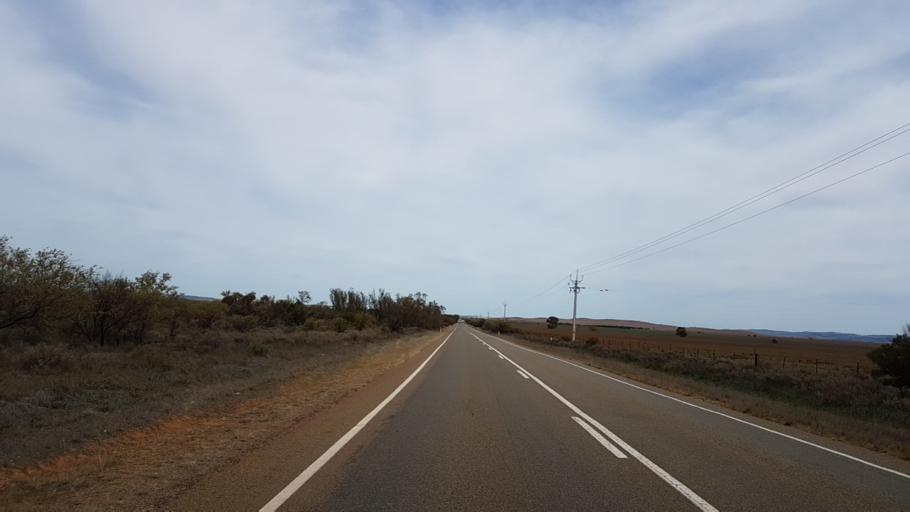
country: AU
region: South Australia
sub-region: Peterborough
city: Peterborough
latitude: -32.9920
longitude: 138.7888
